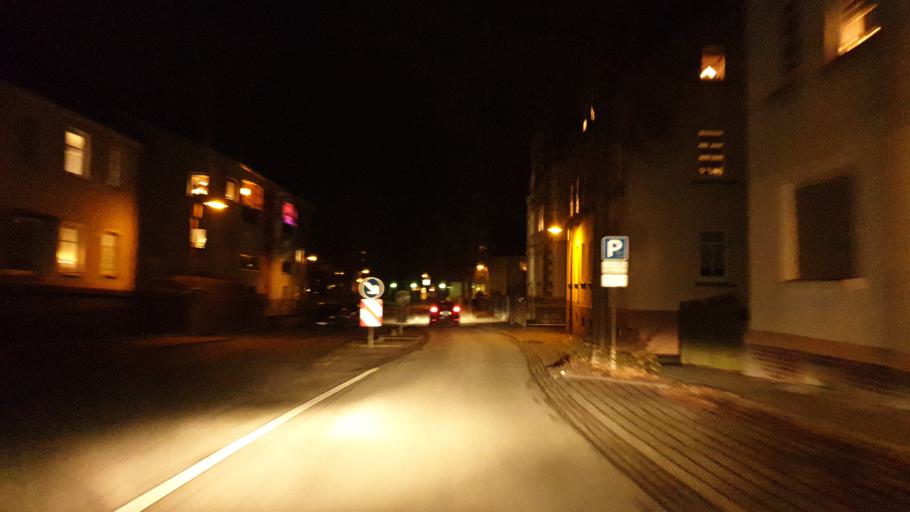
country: DE
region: Saxony
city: Lugau
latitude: 50.7219
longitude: 12.7468
